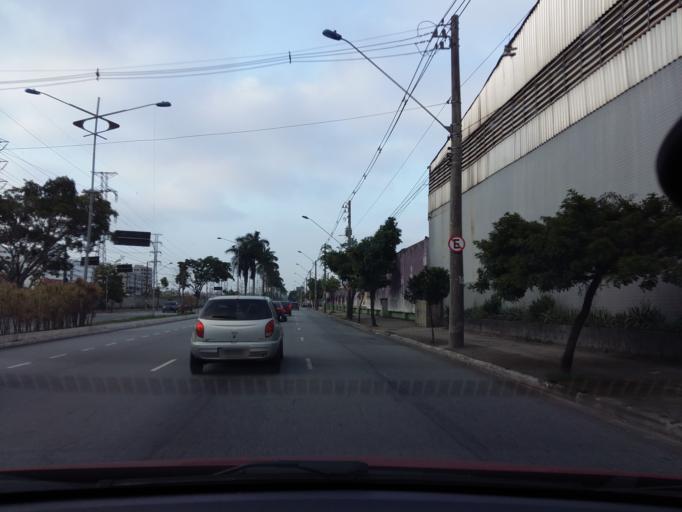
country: BR
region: Sao Paulo
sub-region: Sao Caetano Do Sul
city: Sao Caetano do Sul
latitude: -23.6213
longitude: -46.5817
